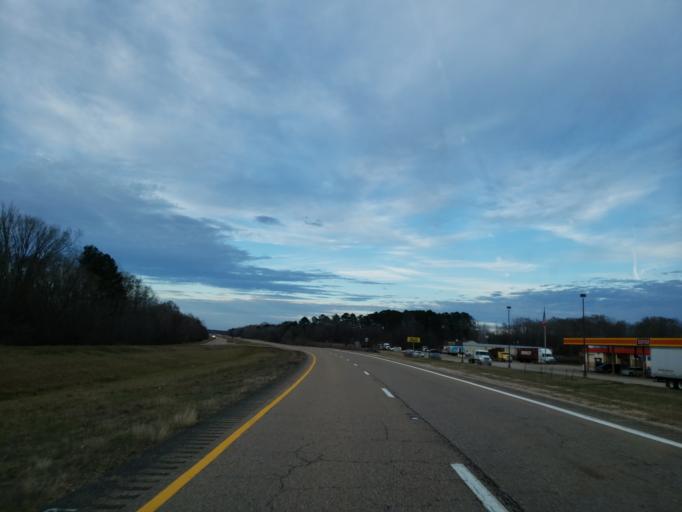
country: US
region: Mississippi
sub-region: Lauderdale County
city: Meridian Station
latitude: 32.5202
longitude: -88.5165
